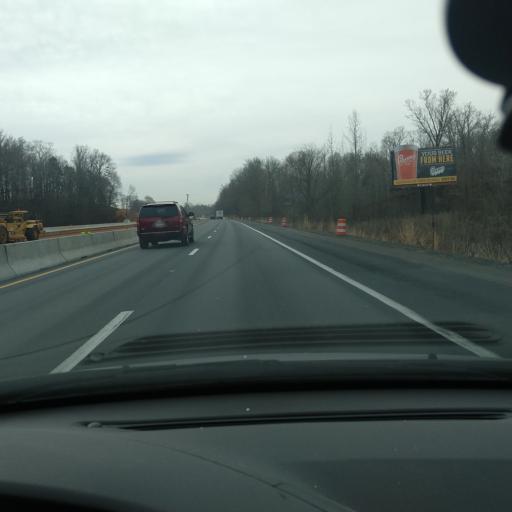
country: US
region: North Carolina
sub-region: Rowan County
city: China Grove
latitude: 35.5384
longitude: -80.5739
